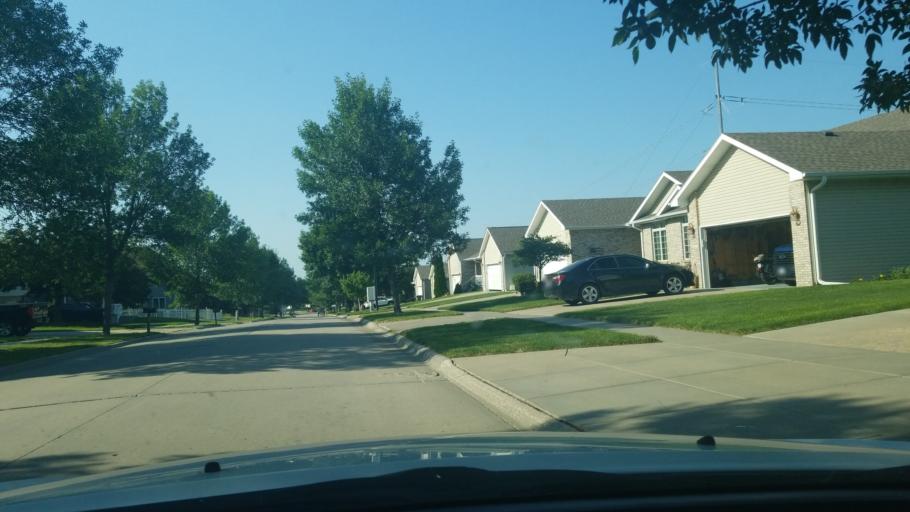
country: US
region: Nebraska
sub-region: Lancaster County
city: Lincoln
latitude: 40.7506
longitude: -96.6110
